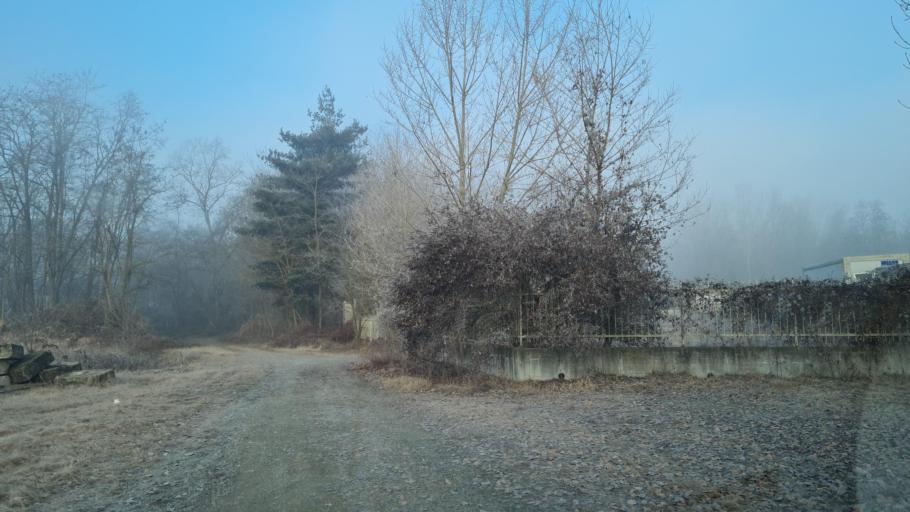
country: IT
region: Piedmont
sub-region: Provincia di Biella
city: Salussola
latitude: 45.4563
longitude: 8.1059
